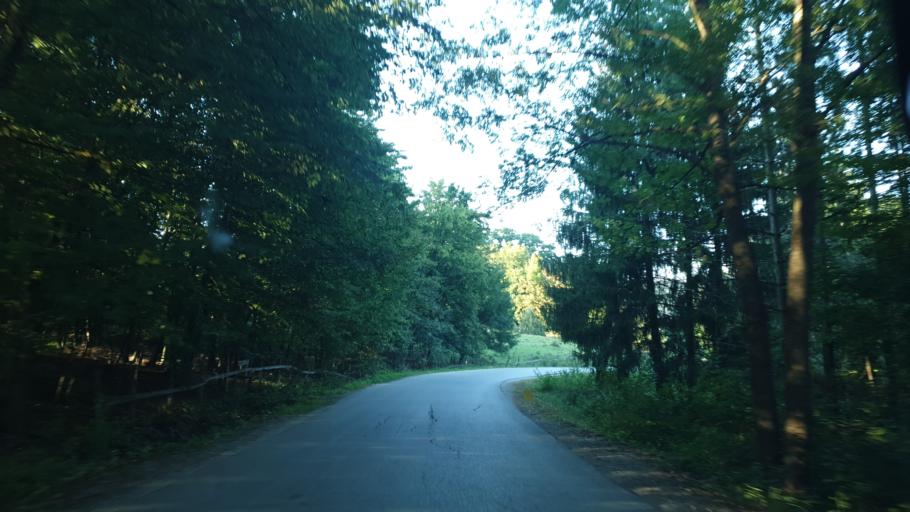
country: RS
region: Central Serbia
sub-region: Zlatiborski Okrug
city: Pozega
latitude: 43.8724
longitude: 19.9914
